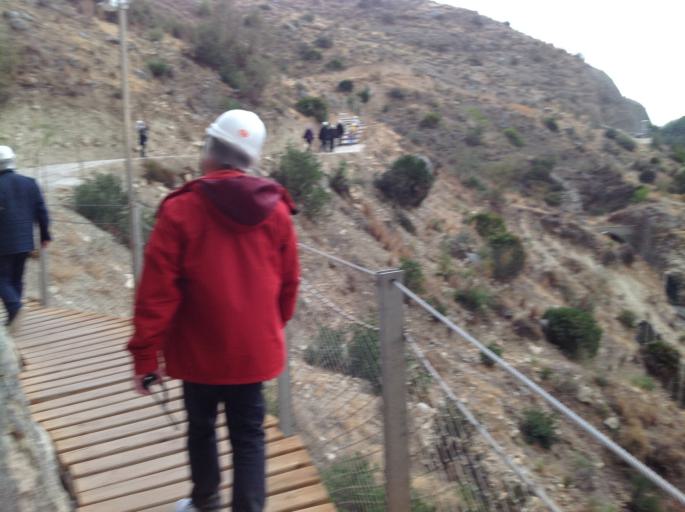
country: ES
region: Andalusia
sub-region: Provincia de Malaga
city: Carratraca
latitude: 36.9162
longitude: -4.7707
